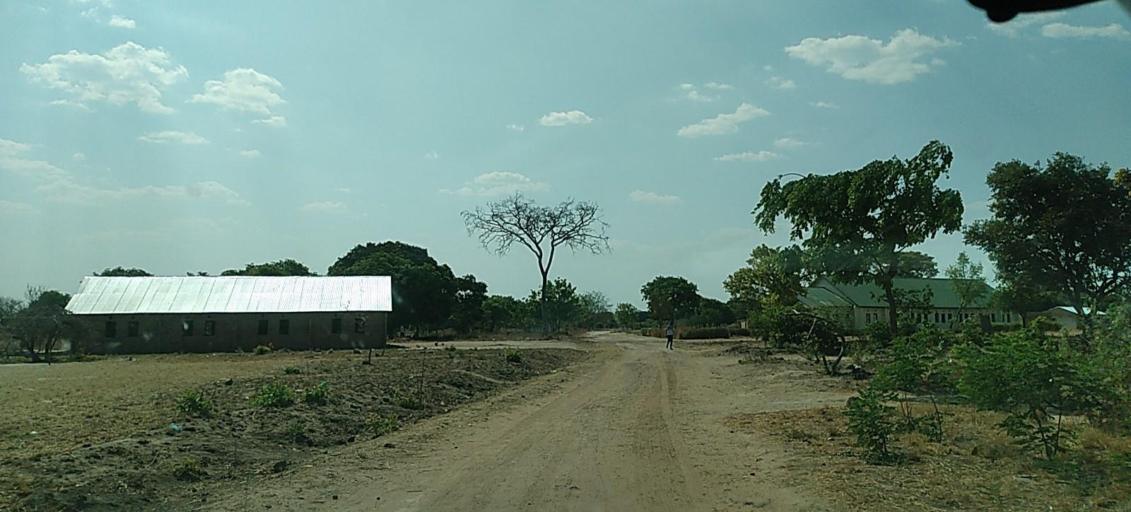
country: ZM
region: North-Western
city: Kalengwa
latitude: -13.1310
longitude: 25.0123
